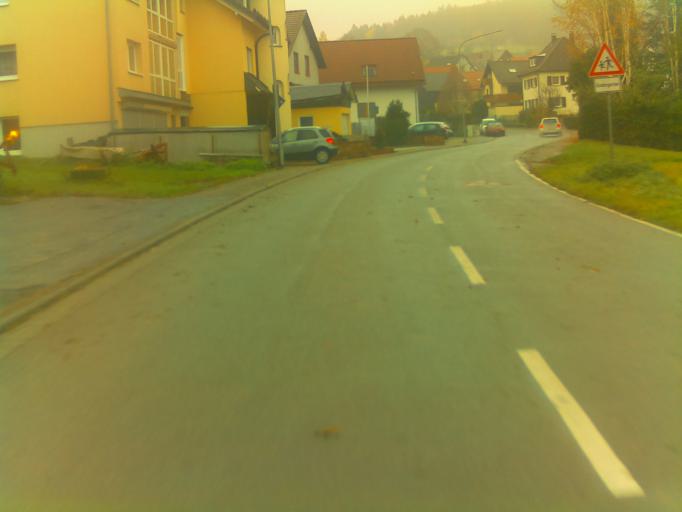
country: DE
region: Hesse
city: Neckarsteinach
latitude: 49.4159
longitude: 8.8510
